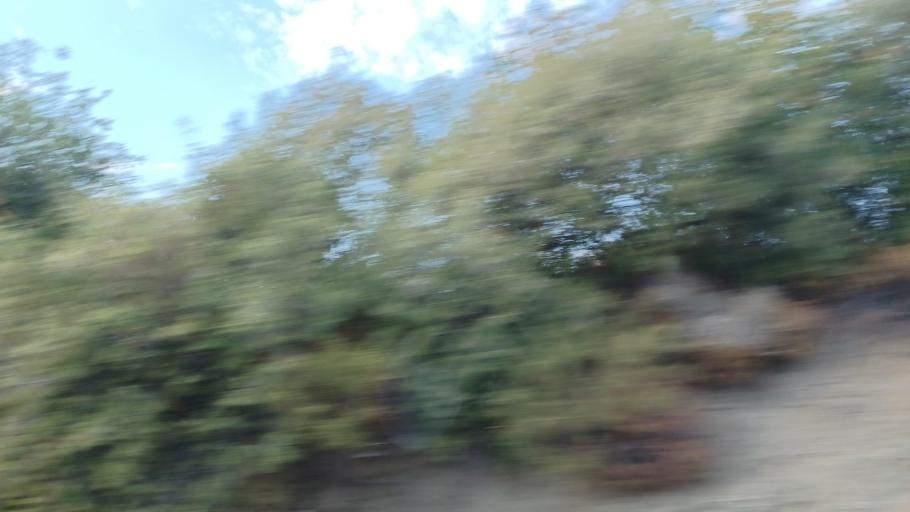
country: CY
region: Limassol
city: Pelendri
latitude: 34.8574
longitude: 32.9196
